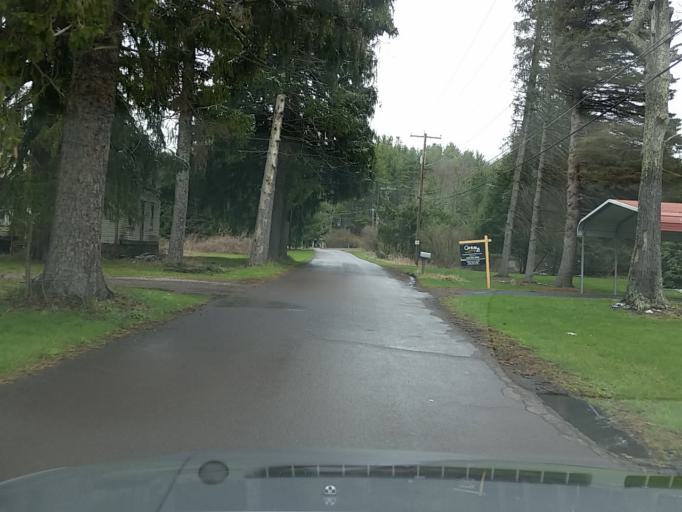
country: US
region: Pennsylvania
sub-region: Sullivan County
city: Laporte
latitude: 41.2778
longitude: -76.3773
